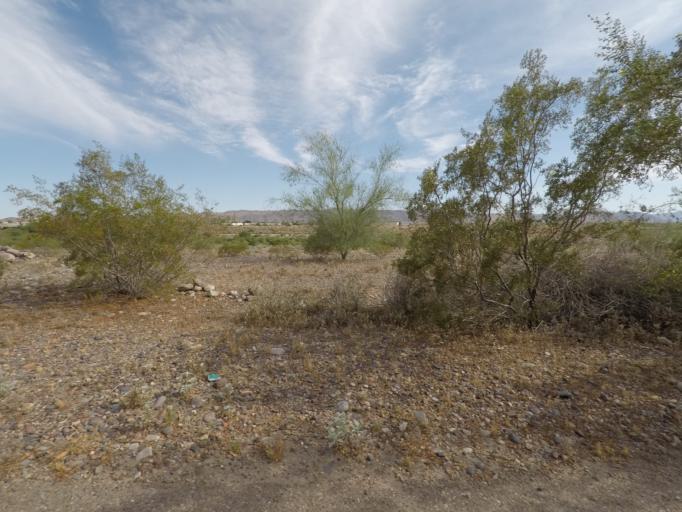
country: US
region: Arizona
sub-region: Maricopa County
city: Phoenix
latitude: 33.4181
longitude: -112.0327
